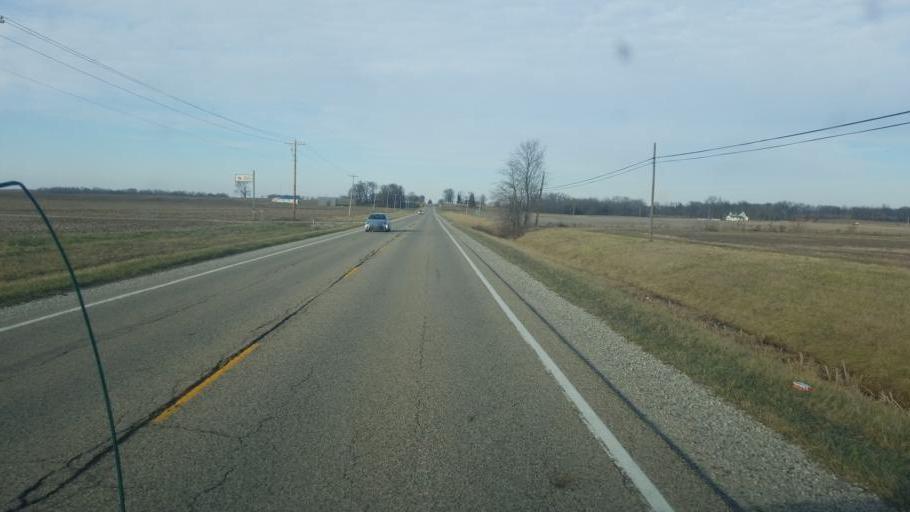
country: US
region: Illinois
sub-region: Lawrence County
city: Bridgeport
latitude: 38.6039
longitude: -87.6943
